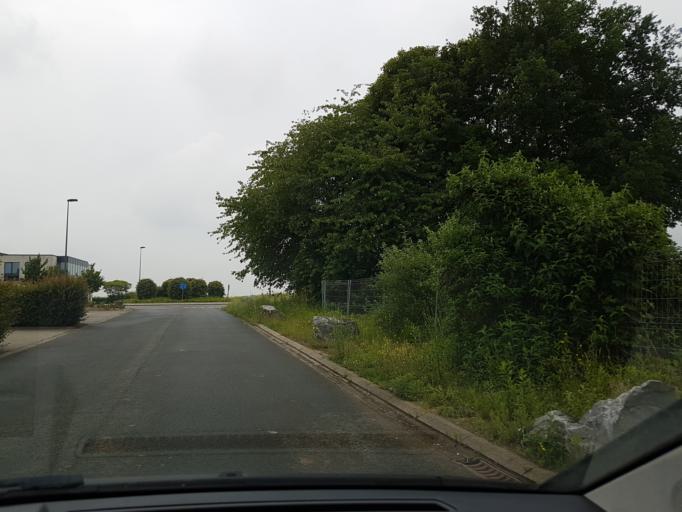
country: BE
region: Flanders
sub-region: Provincie Vlaams-Brabant
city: Zaventem
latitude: 50.8770
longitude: 4.4940
